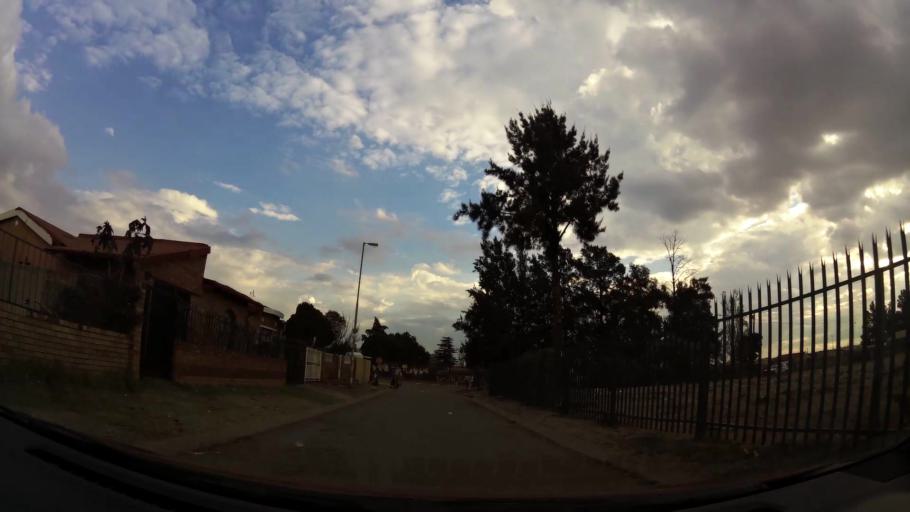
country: ZA
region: Gauteng
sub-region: City of Johannesburg Metropolitan Municipality
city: Soweto
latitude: -26.2406
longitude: 27.8259
